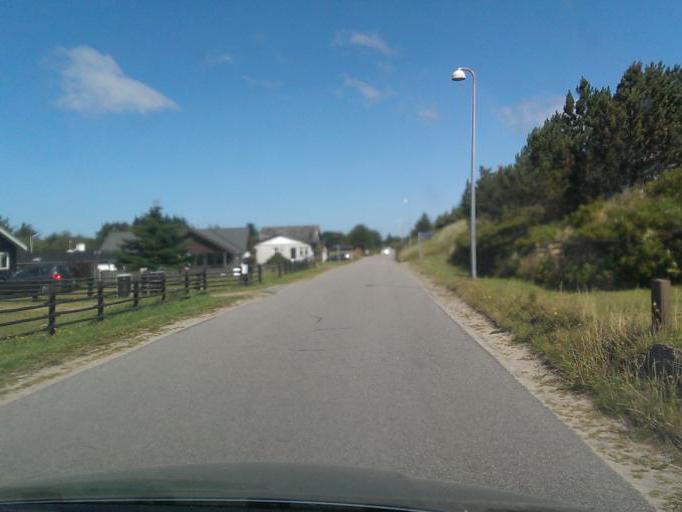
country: DK
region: North Denmark
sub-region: Jammerbugt Kommune
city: Pandrup
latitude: 57.2522
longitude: 9.5918
